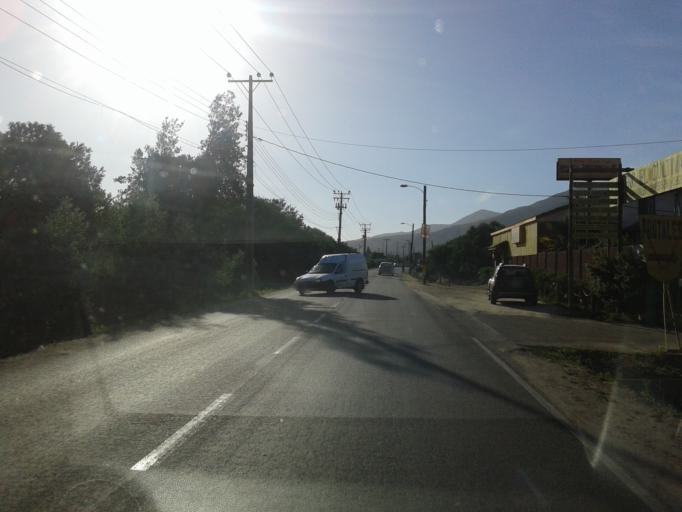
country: CL
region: Valparaiso
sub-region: Provincia de Quillota
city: Quillota
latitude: -32.8585
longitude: -71.2260
